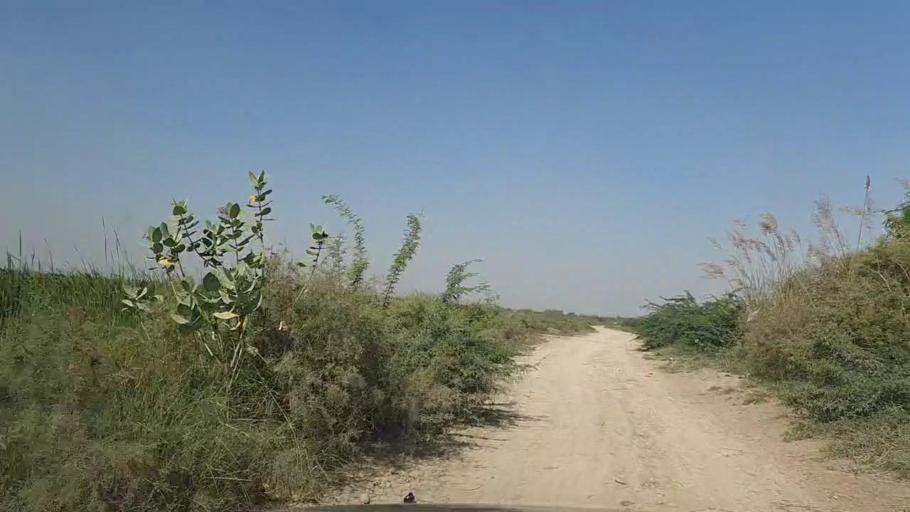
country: PK
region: Sindh
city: Daro Mehar
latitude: 24.8207
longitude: 68.1503
